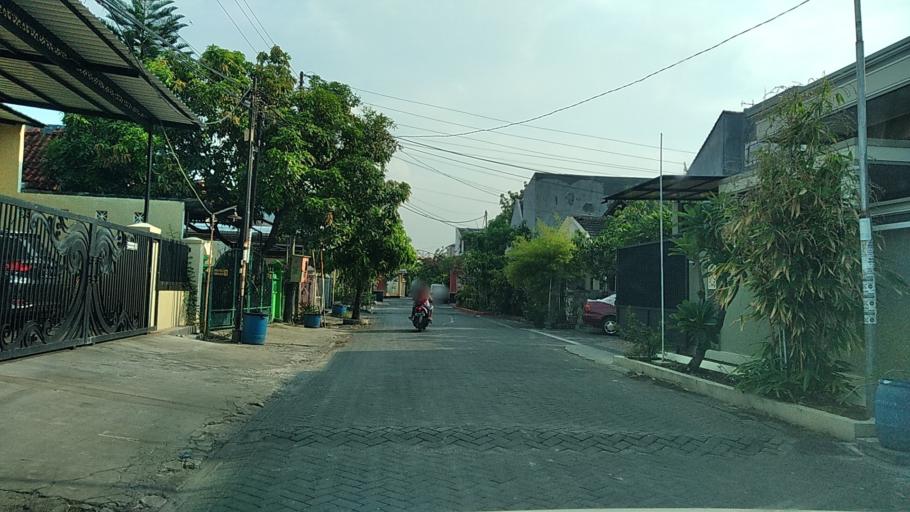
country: ID
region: Central Java
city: Semarang
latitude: -6.9901
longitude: 110.4653
